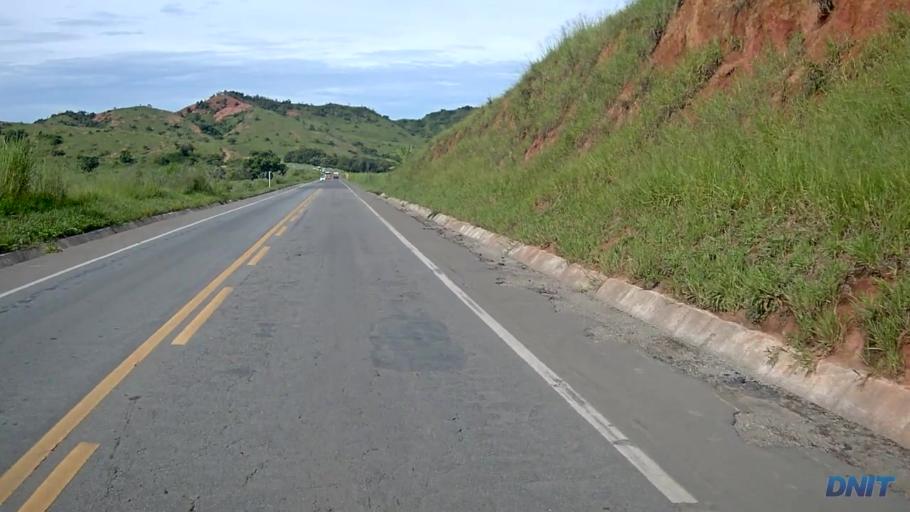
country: BR
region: Minas Gerais
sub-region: Belo Oriente
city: Belo Oriente
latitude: -19.2211
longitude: -42.3119
